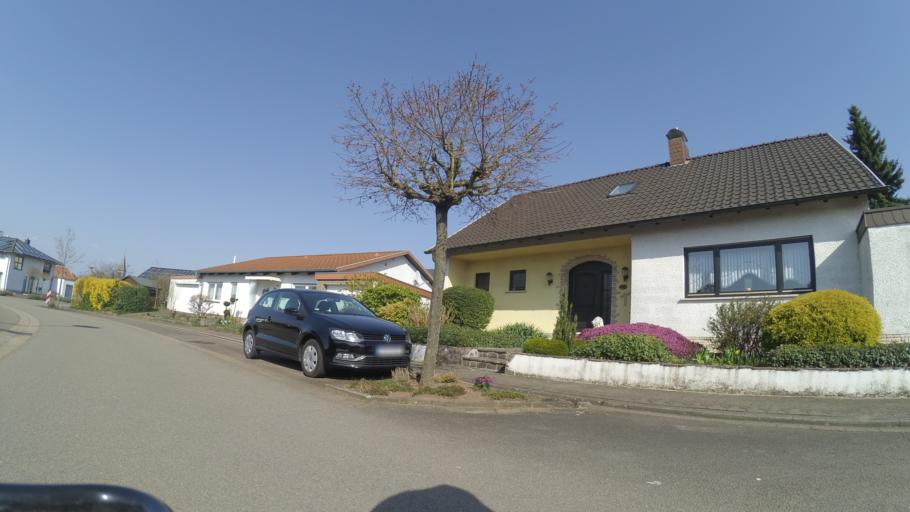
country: DE
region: Saarland
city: Quierschied
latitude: 49.3278
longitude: 6.9907
